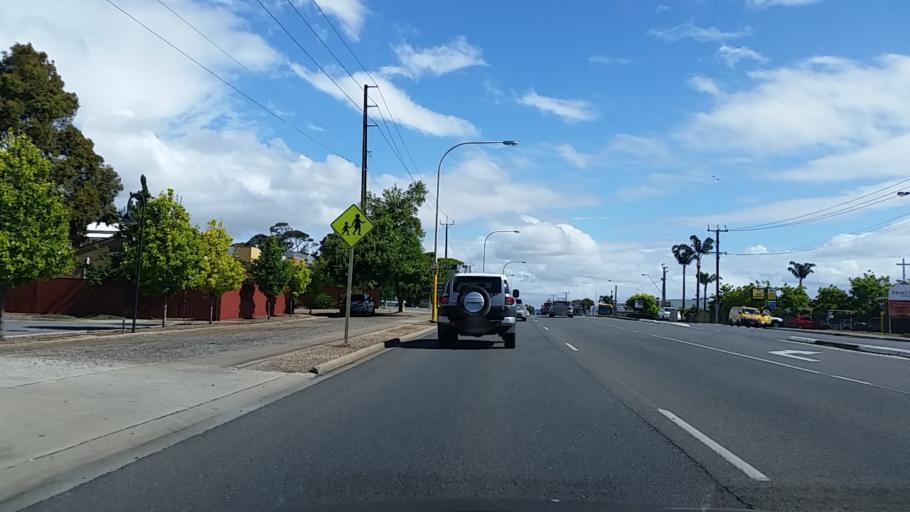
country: AU
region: South Australia
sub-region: Adelaide
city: Port Noarlunga
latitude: -35.1365
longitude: 138.4862
